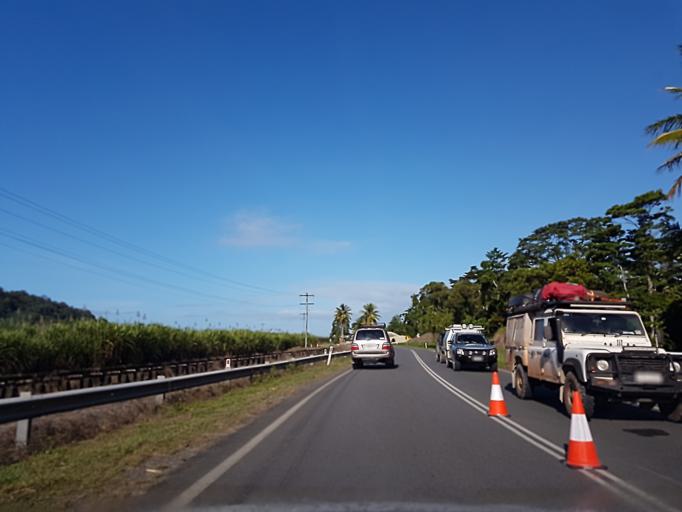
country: AU
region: Queensland
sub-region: Cairns
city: Port Douglas
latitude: -16.3914
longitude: 145.3966
